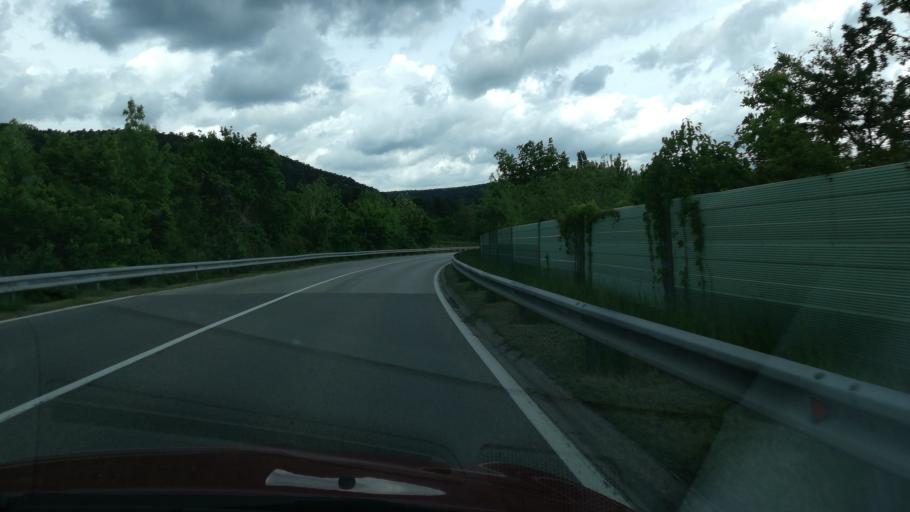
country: AT
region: Lower Austria
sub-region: Politischer Bezirk Baden
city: Baden
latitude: 47.9994
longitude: 16.2106
